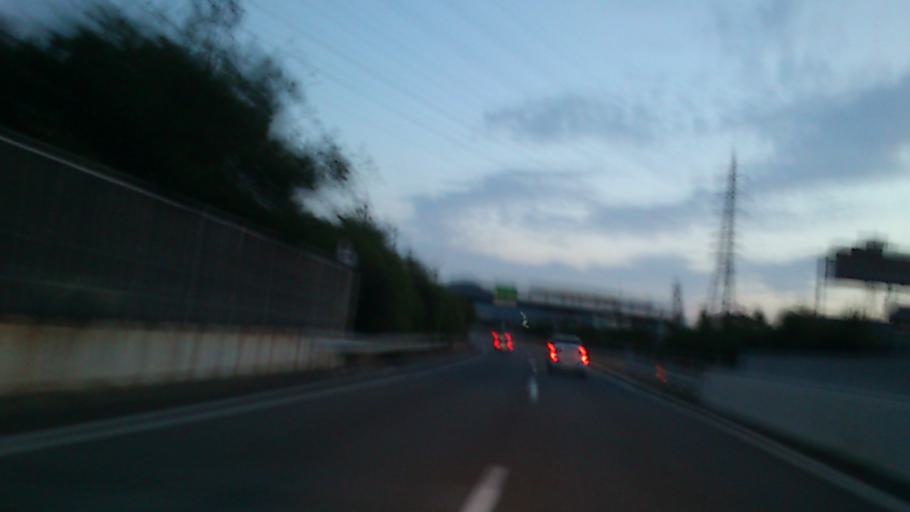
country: JP
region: Gifu
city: Tajimi
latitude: 35.3469
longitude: 137.1034
